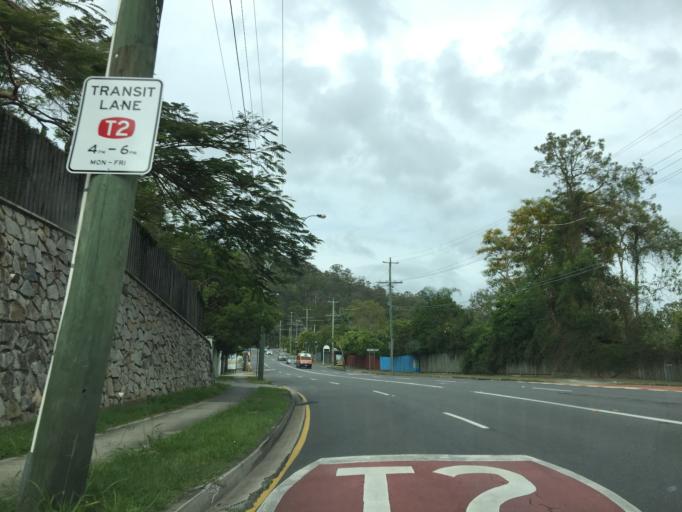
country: AU
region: Queensland
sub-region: Brisbane
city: Milton
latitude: -27.4482
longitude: 152.9697
